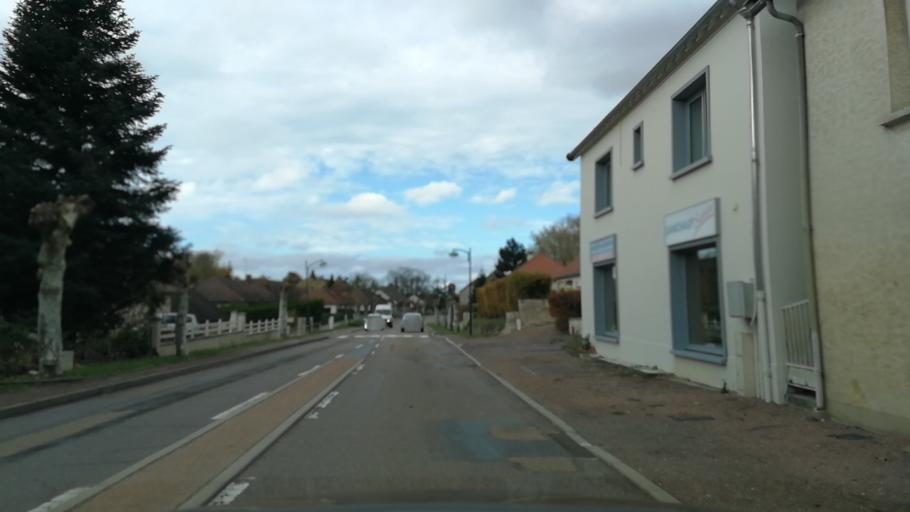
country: FR
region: Bourgogne
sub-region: Departement de la Cote-d'Or
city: Pouilly-en-Auxois
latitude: 47.2564
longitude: 4.5619
